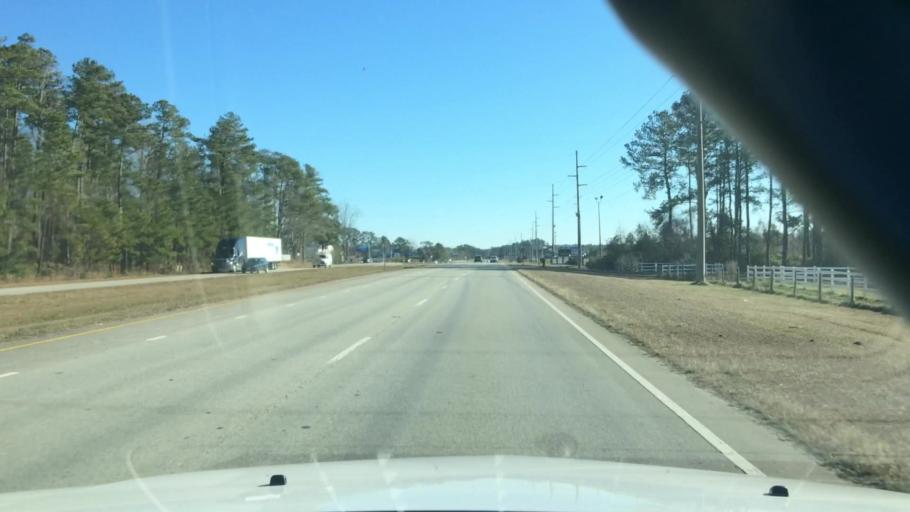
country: US
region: North Carolina
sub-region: Brunswick County
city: Shallotte
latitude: 33.9561
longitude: -78.4384
